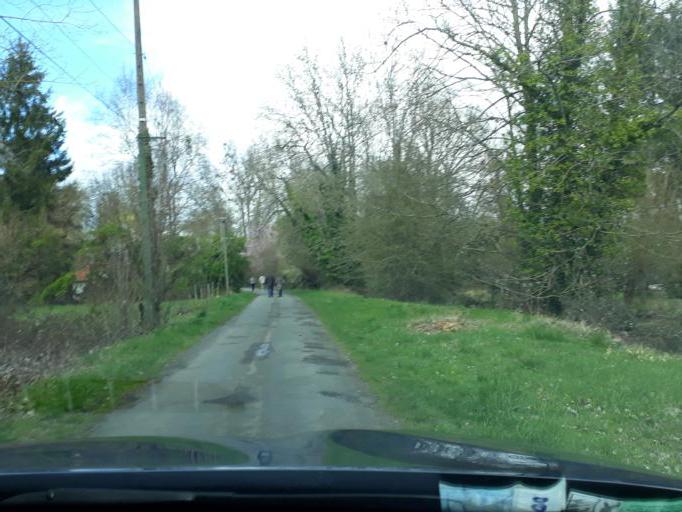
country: FR
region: Centre
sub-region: Departement du Loiret
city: Meung-sur-Loire
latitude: 47.8341
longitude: 1.7020
